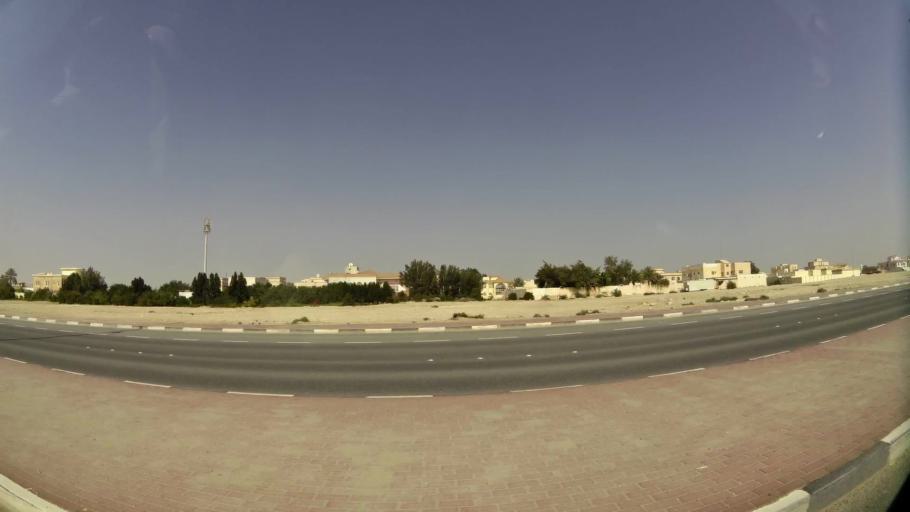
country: QA
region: Baladiyat Umm Salal
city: Umm Salal Muhammad
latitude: 25.3710
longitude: 51.4344
